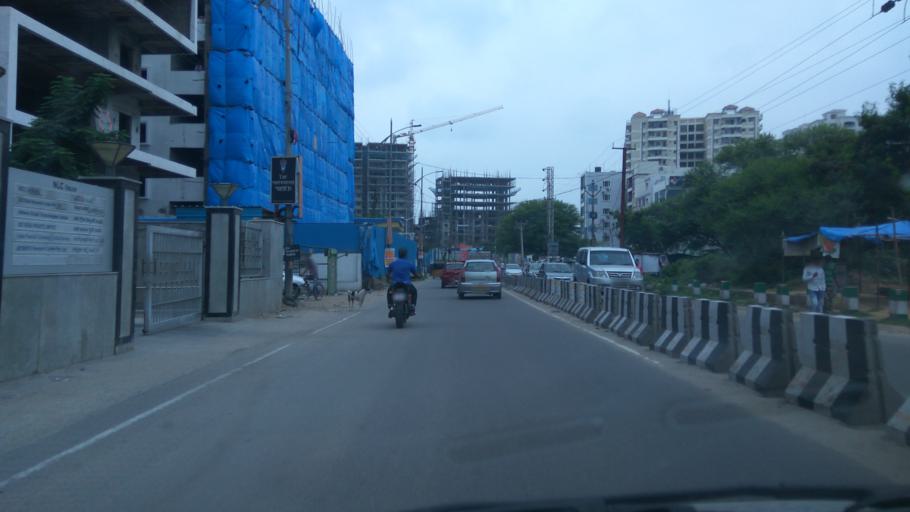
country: IN
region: Telangana
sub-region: Rangareddi
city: Kukatpalli
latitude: 17.4365
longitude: 78.3884
